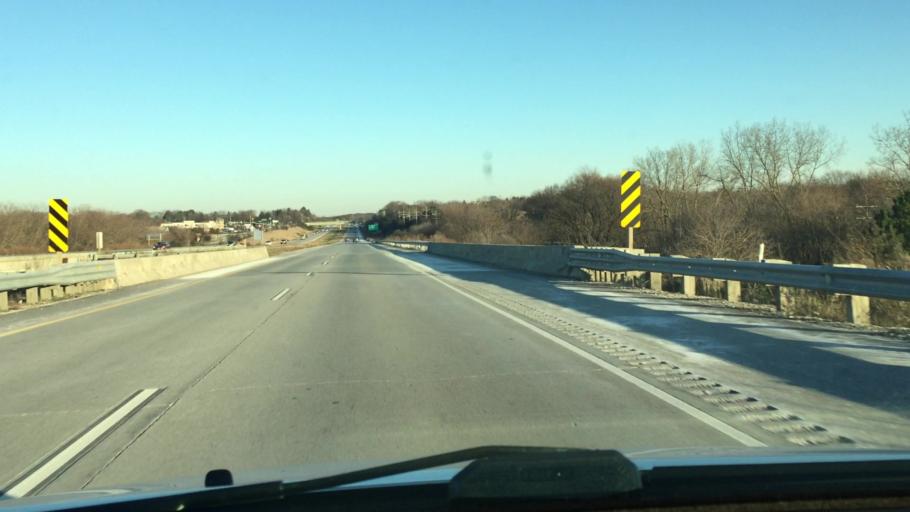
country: US
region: Wisconsin
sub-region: Waukesha County
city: Hartland
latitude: 43.1096
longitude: -88.3461
